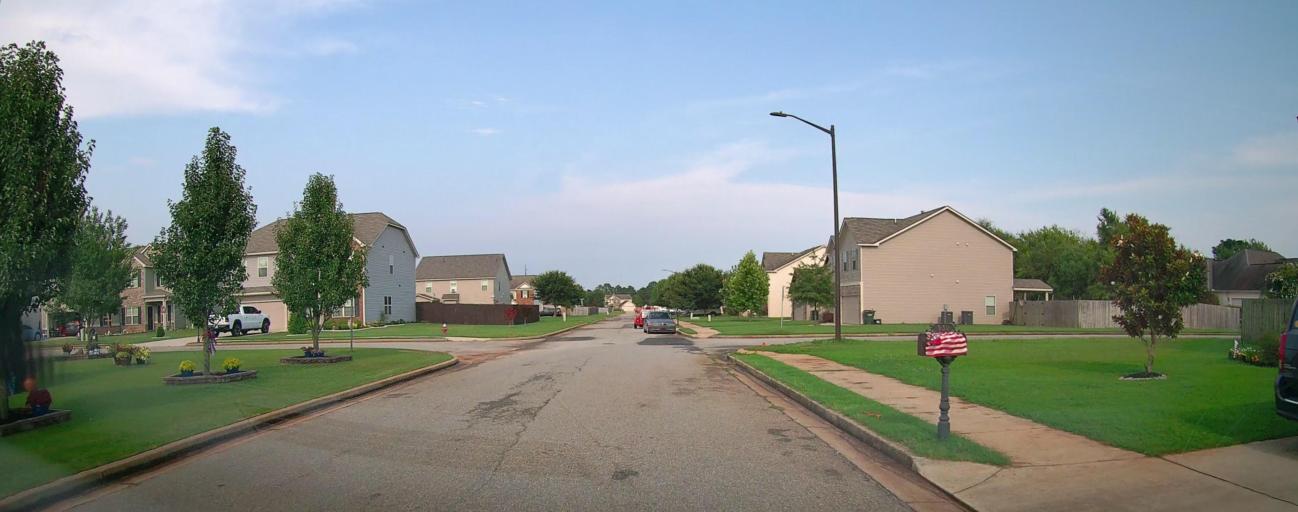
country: US
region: Georgia
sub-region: Houston County
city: Centerville
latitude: 32.6438
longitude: -83.7135
